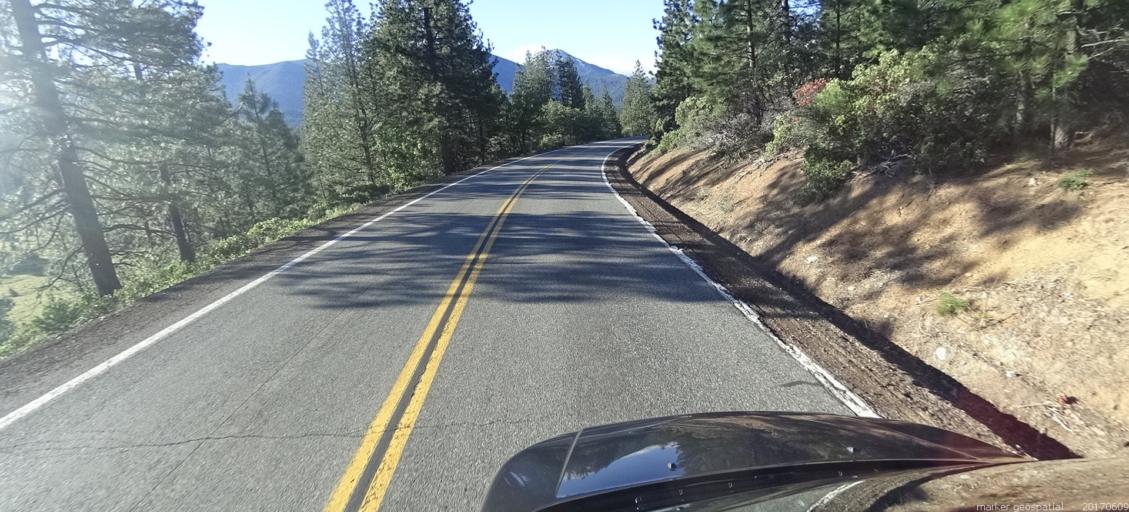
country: US
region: California
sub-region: Siskiyou County
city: Weed
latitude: 41.4289
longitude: -122.6373
